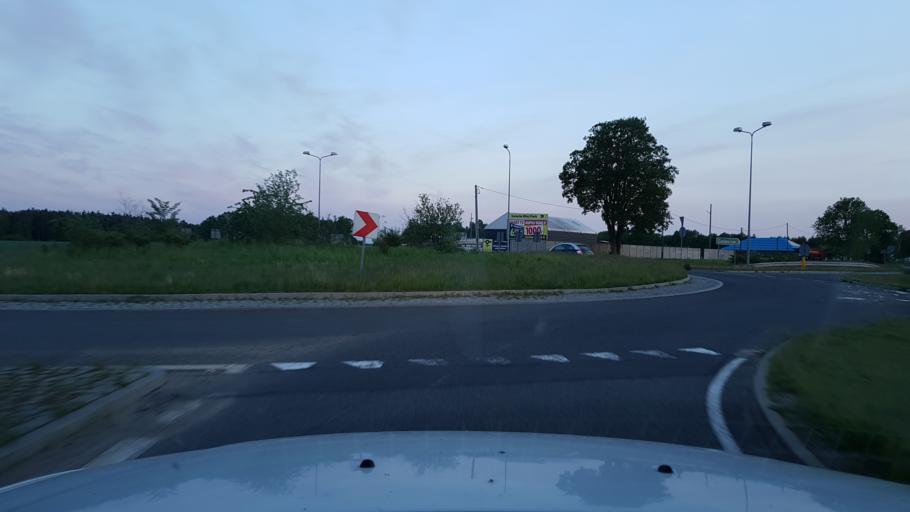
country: PL
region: West Pomeranian Voivodeship
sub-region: Powiat goleniowski
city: Goleniow
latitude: 53.5661
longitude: 14.8693
